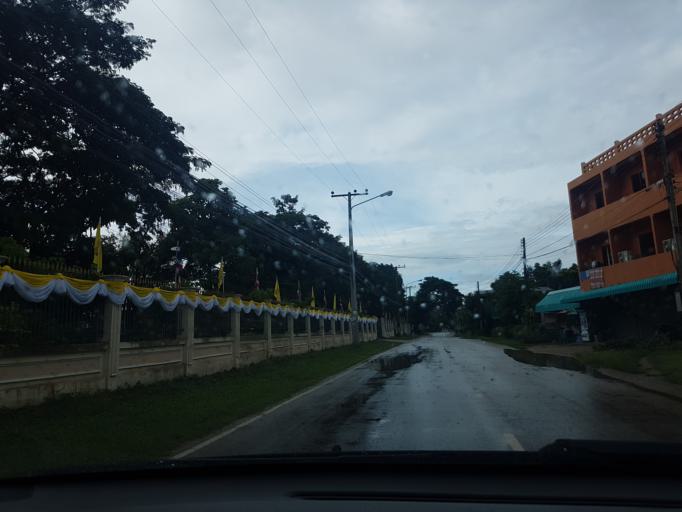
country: TH
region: Lampang
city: Lampang
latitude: 18.3064
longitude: 99.4770
